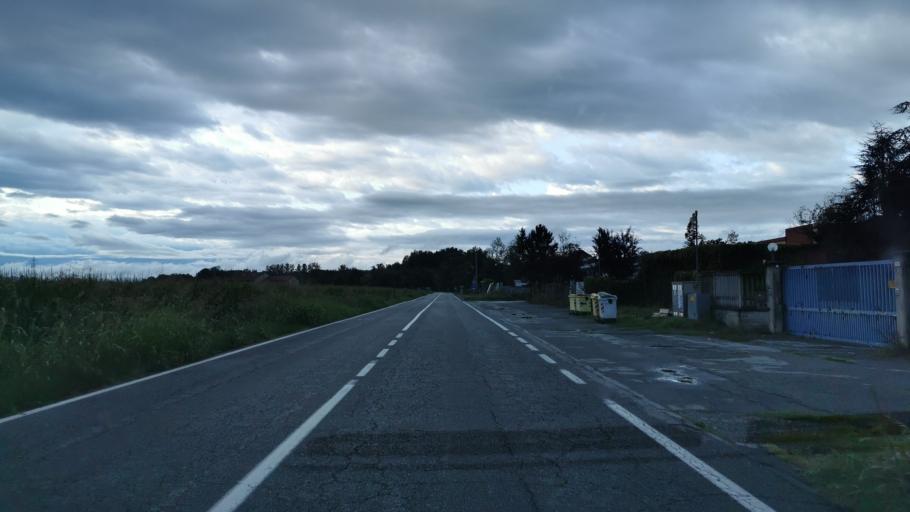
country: IT
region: Piedmont
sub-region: Provincia di Torino
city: San Benigno Canavese
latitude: 45.2240
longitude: 7.7608
